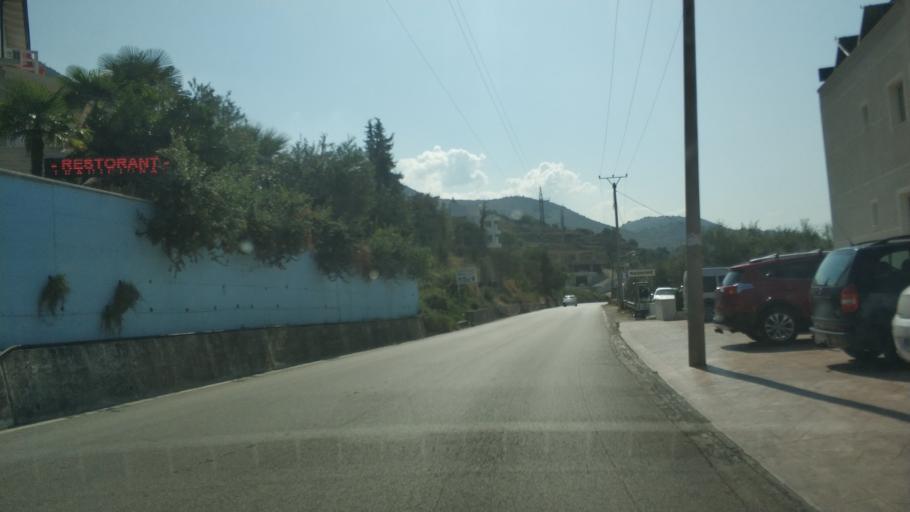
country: AL
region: Vlore
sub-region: Rrethi i Vlores
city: Orikum
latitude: 40.3917
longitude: 19.4808
